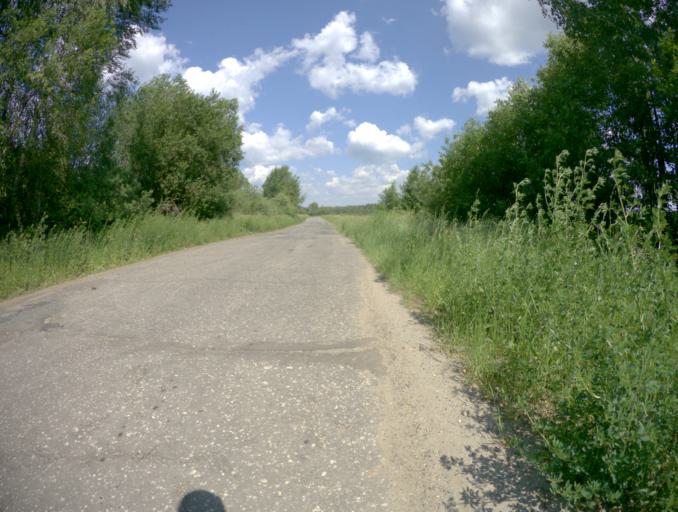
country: RU
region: Vladimir
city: Vyazniki
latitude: 56.3159
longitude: 42.1264
